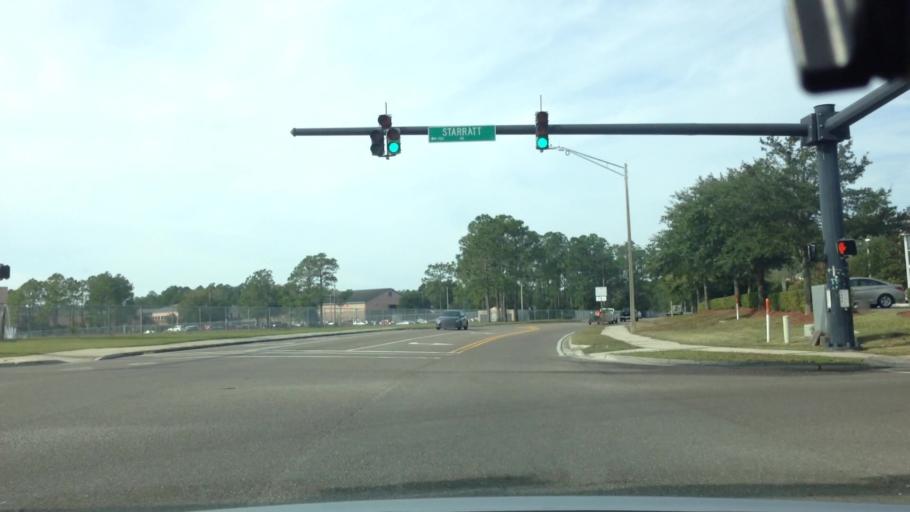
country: US
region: Florida
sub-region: Nassau County
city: Yulee
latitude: 30.4838
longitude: -81.6040
